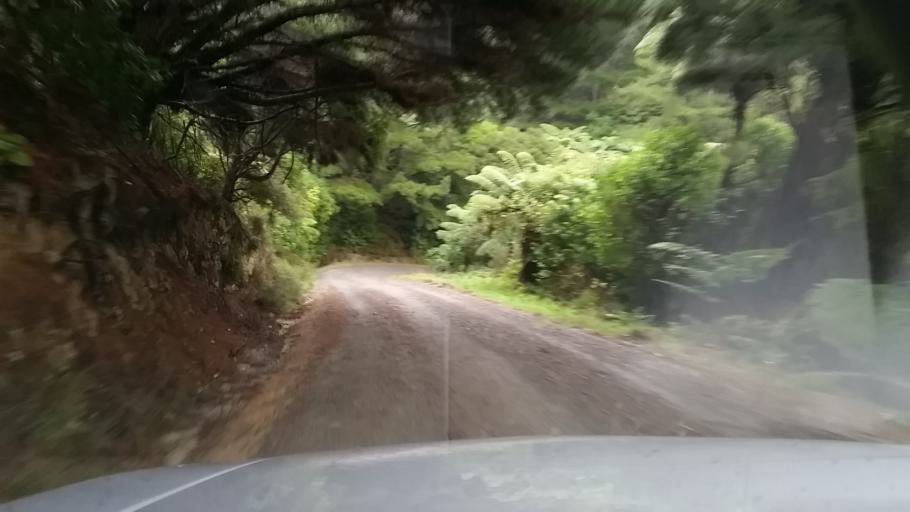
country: NZ
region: Marlborough
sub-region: Marlborough District
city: Picton
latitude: -41.1334
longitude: 174.0435
